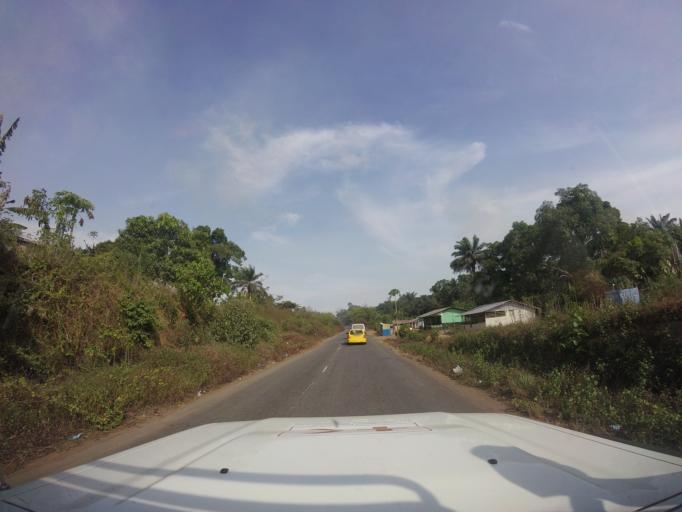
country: LR
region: Bomi
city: Tubmanburg
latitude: 6.6985
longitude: -10.9104
